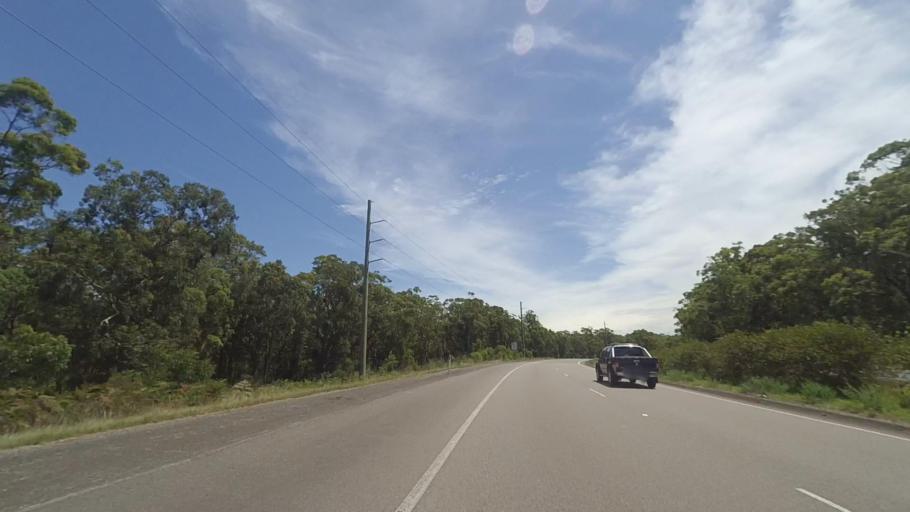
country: AU
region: New South Wales
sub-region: Port Stephens Shire
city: Anna Bay
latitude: -32.7780
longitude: 152.0031
